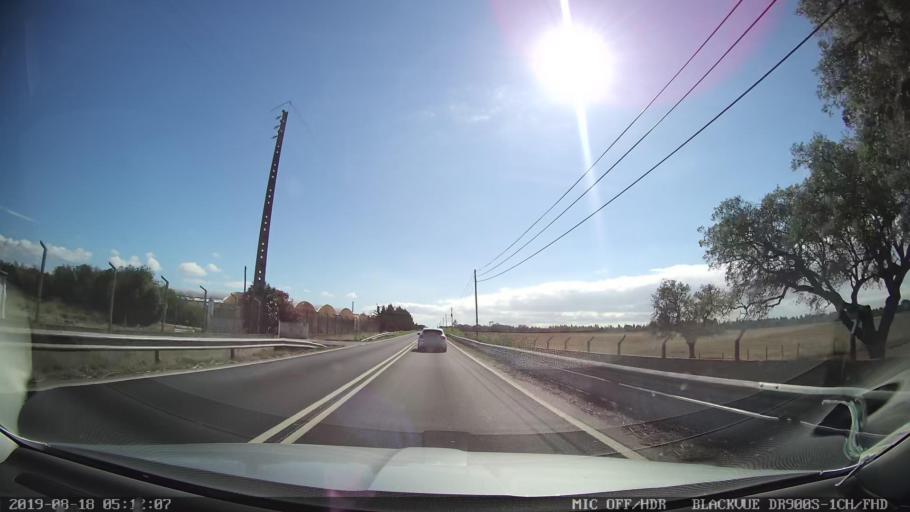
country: PT
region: Setubal
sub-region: Alcochete
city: Alcochete
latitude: 38.7710
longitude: -8.8940
